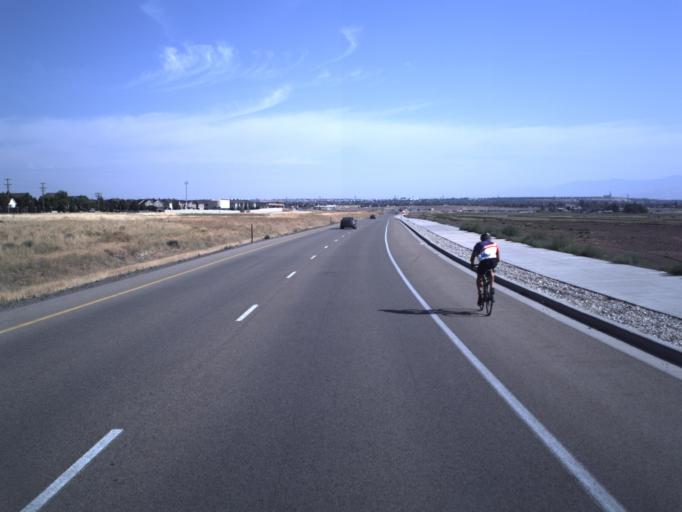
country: US
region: Utah
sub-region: Salt Lake County
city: Herriman
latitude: 40.4969
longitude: -112.0038
